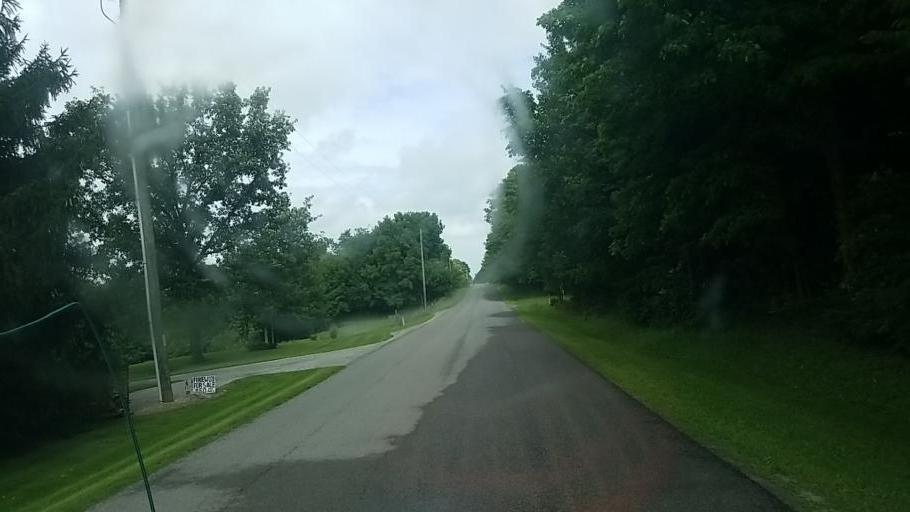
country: US
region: Ohio
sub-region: Champaign County
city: North Lewisburg
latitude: 40.2606
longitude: -83.6250
